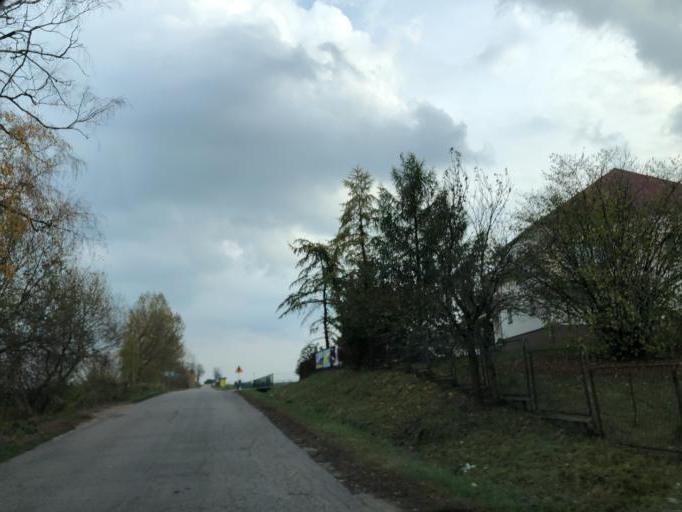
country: PL
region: Podlasie
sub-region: Lomza
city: Lomza
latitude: 53.1206
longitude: 22.0152
